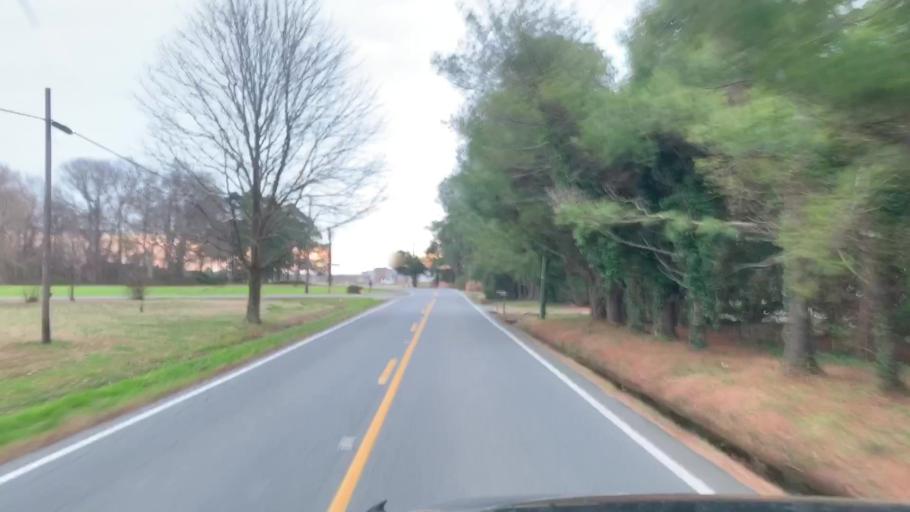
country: US
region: North Carolina
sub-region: Currituck County
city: Moyock
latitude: 36.6245
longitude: -76.1602
